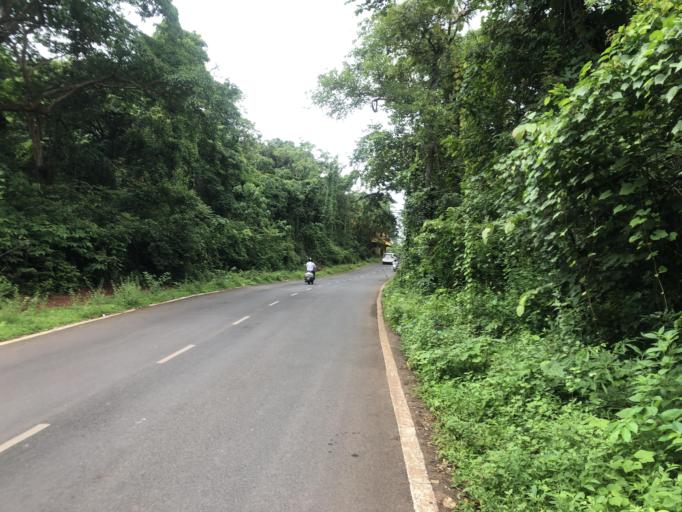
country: IN
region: Goa
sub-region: North Goa
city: Serula
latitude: 15.5415
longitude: 73.8318
